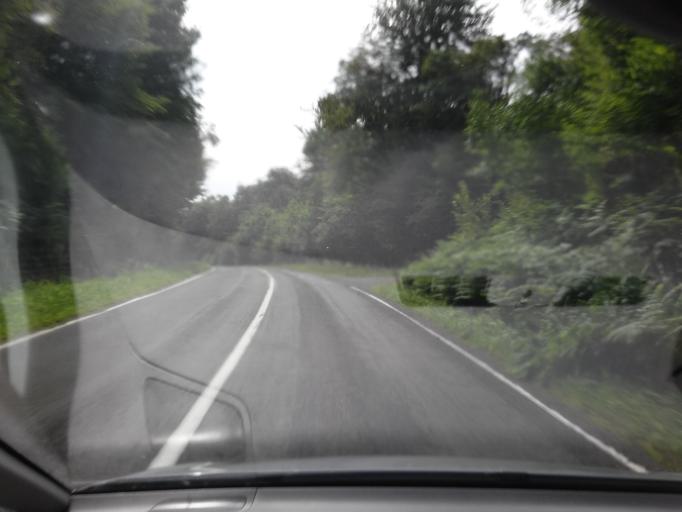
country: BE
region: Wallonia
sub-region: Province du Luxembourg
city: Chiny
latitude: 49.7762
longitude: 5.3503
